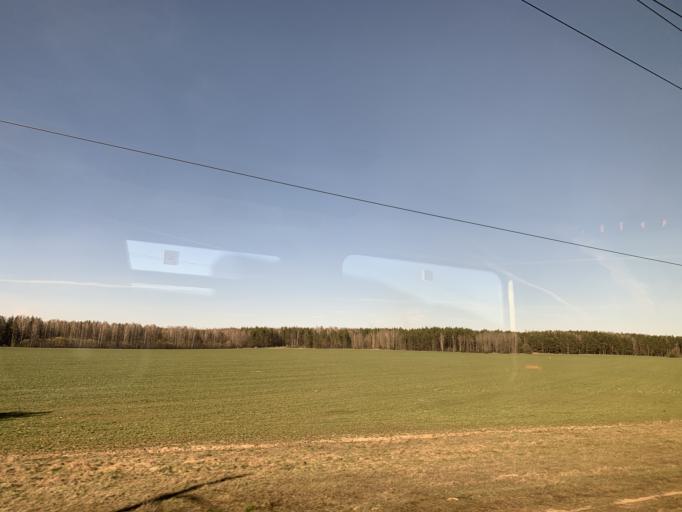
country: BY
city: Soly
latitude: 54.4952
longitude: 26.2739
